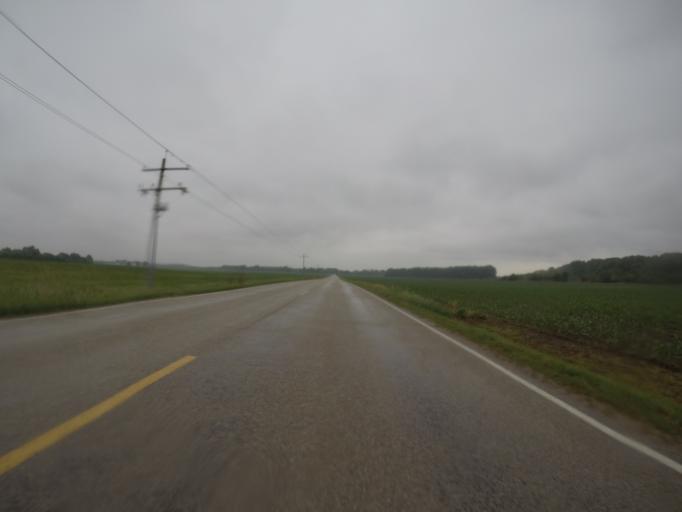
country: US
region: Kansas
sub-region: Pottawatomie County
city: Wamego
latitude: 39.2243
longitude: -96.2312
